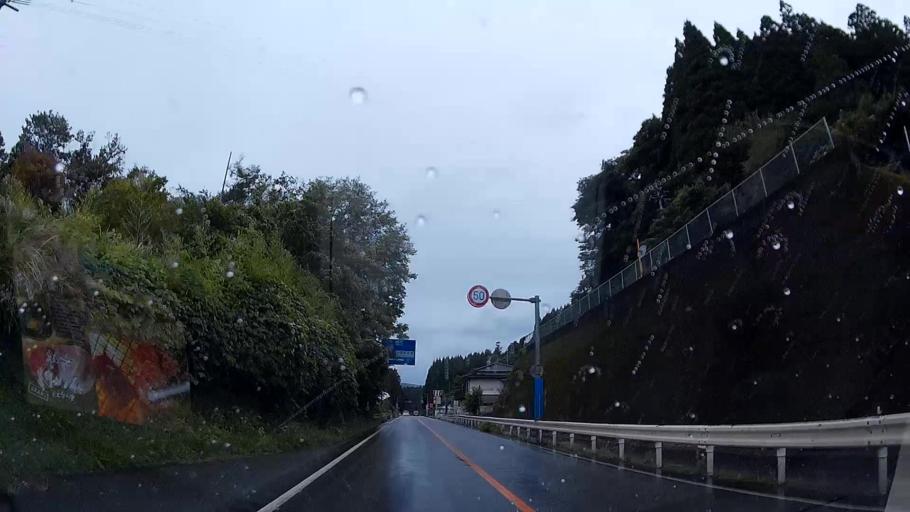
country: JP
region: Oita
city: Tsukawaki
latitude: 33.1292
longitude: 131.0630
